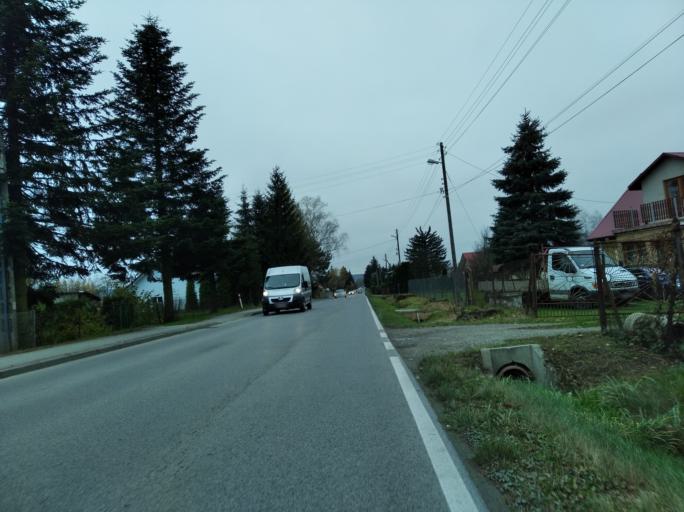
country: PL
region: Subcarpathian Voivodeship
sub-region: Powiat krosnienski
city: Chorkowka
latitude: 49.6750
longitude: 21.7024
